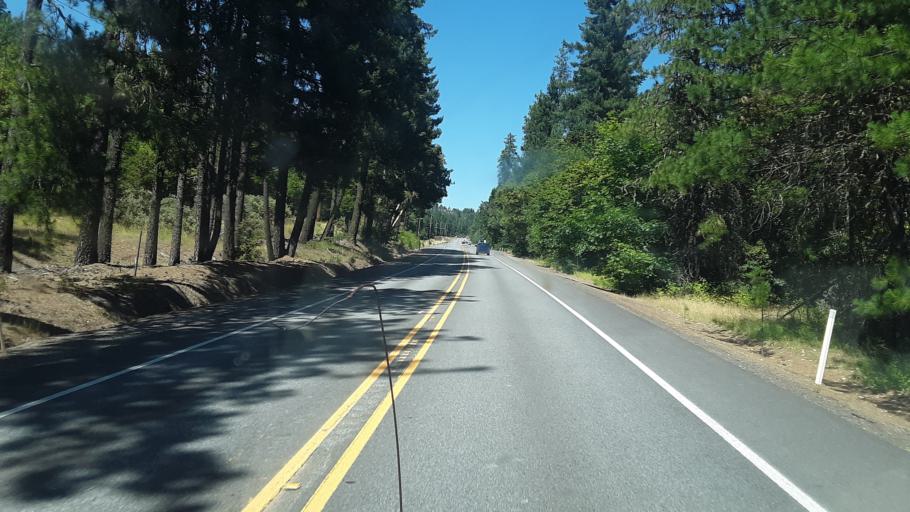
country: US
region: Oregon
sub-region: Josephine County
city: Cave Junction
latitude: 42.3206
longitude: -123.5987
